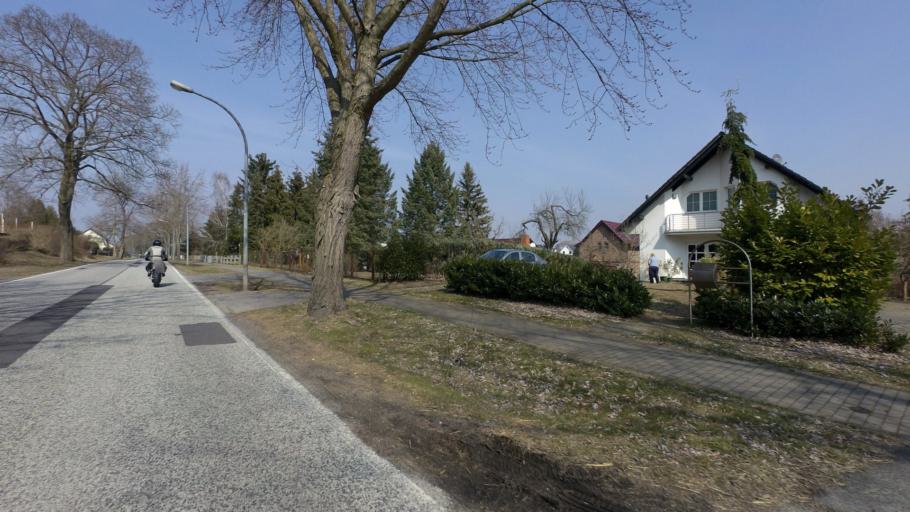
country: DE
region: Brandenburg
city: Werder
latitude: 52.4223
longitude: 12.8914
